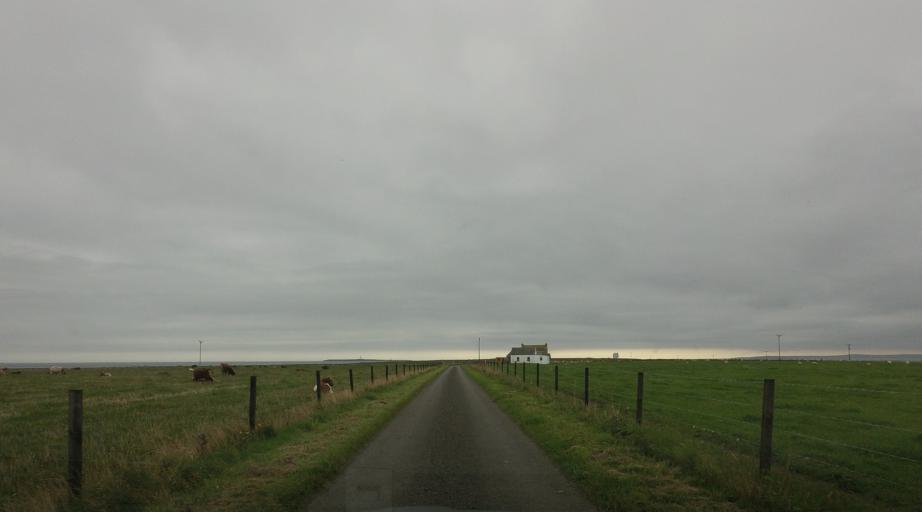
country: GB
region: Scotland
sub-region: Orkney Islands
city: Orkney
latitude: 58.7360
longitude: -2.9593
